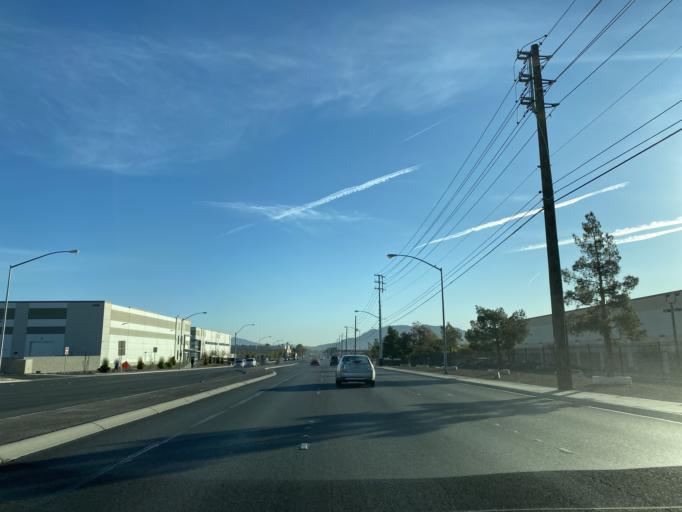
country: US
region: Nevada
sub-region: Clark County
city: Nellis Air Force Base
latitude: 36.2403
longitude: -115.0771
